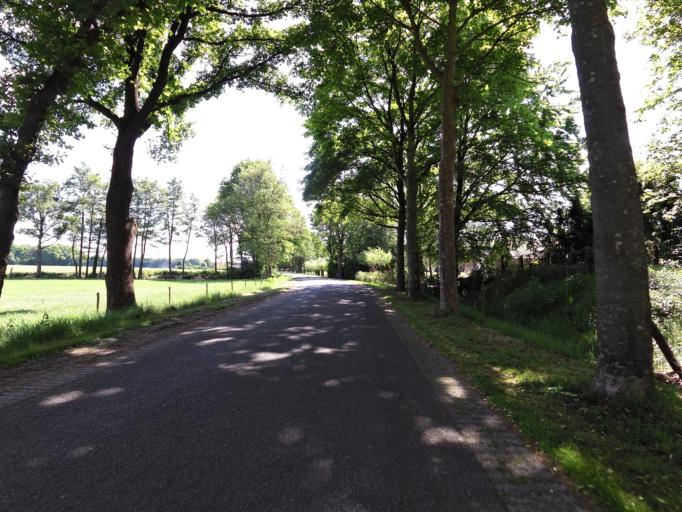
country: NL
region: Gelderland
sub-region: Gemeente Bronckhorst
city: Zelhem
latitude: 52.0572
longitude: 6.3796
